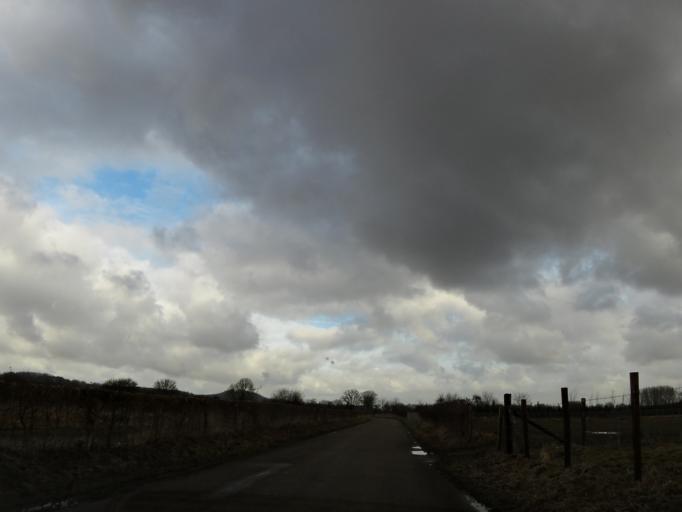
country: NL
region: Limburg
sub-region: Eijsden-Margraten
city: Eijsden
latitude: 50.7861
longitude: 5.7014
